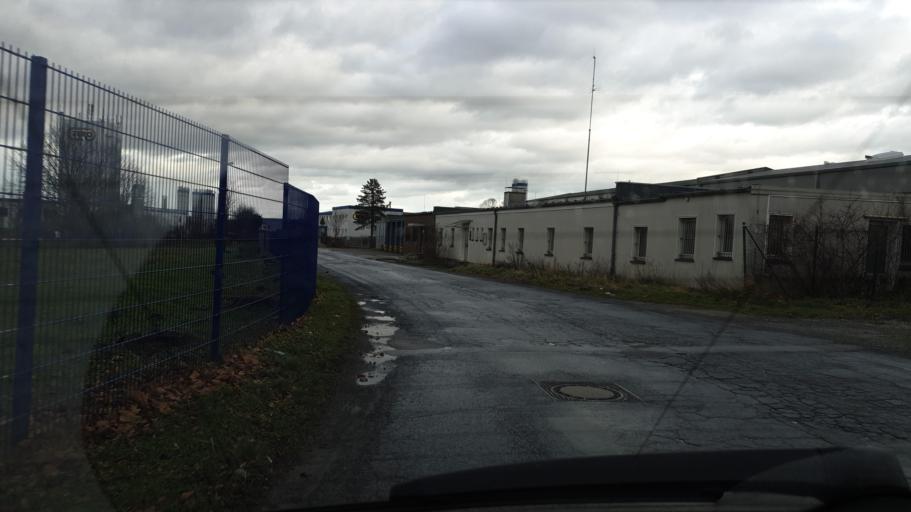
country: DE
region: North Rhine-Westphalia
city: Bad Oeynhausen
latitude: 52.1801
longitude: 8.8106
